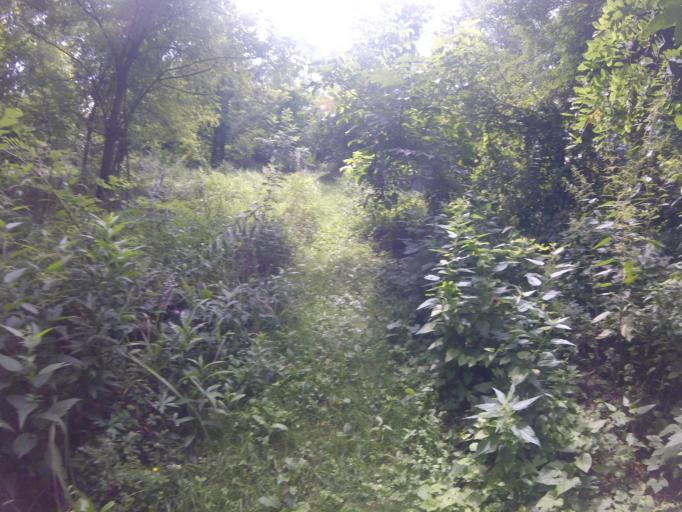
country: HU
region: Zala
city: Lenti
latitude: 46.5742
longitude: 16.6078
